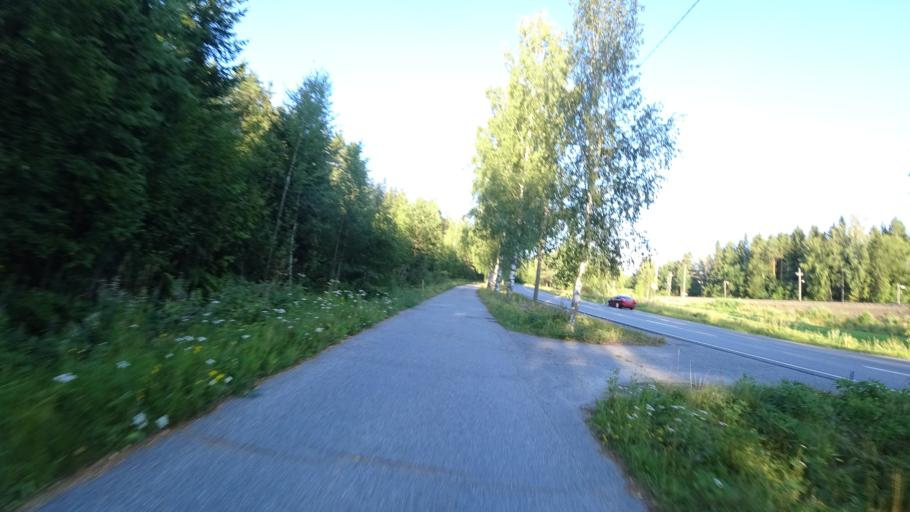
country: FI
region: Pirkanmaa
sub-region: Tampere
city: Nokia
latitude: 61.4666
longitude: 23.4236
